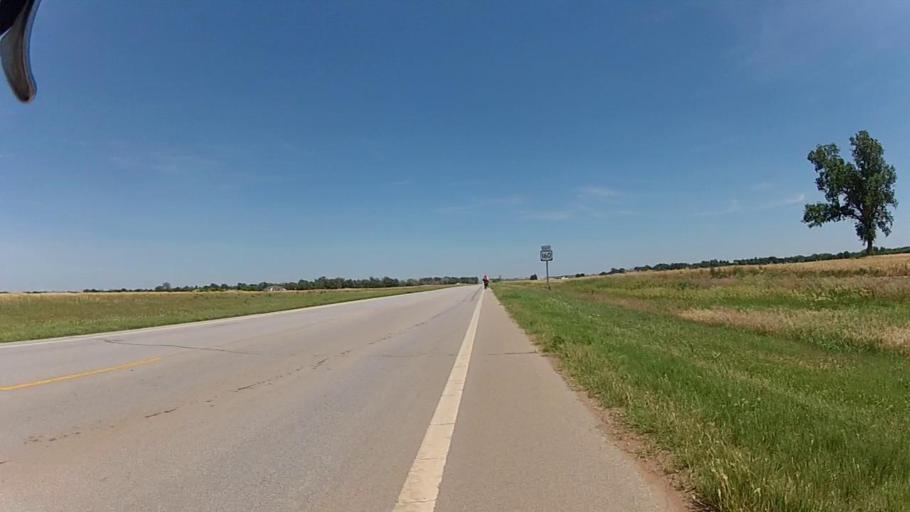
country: US
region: Kansas
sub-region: Harper County
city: Harper
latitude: 37.2387
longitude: -98.1296
